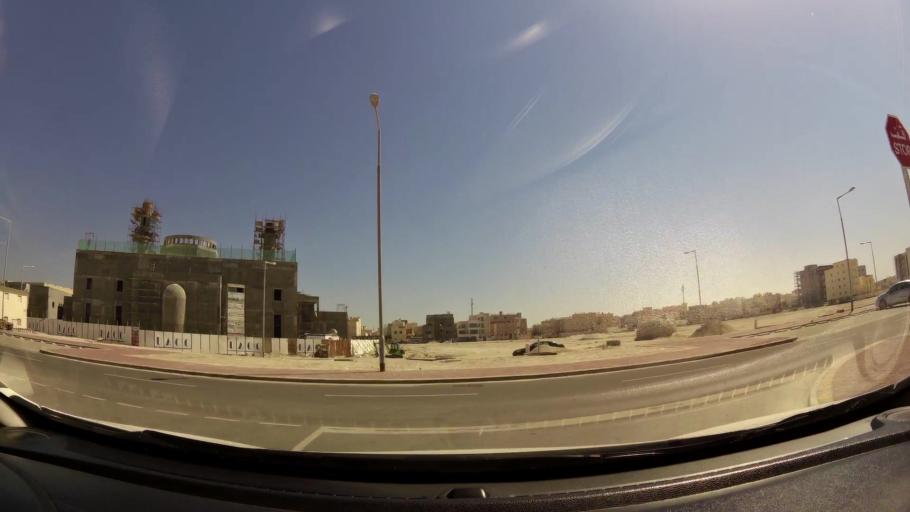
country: BH
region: Muharraq
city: Al Muharraq
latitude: 26.2758
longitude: 50.5983
